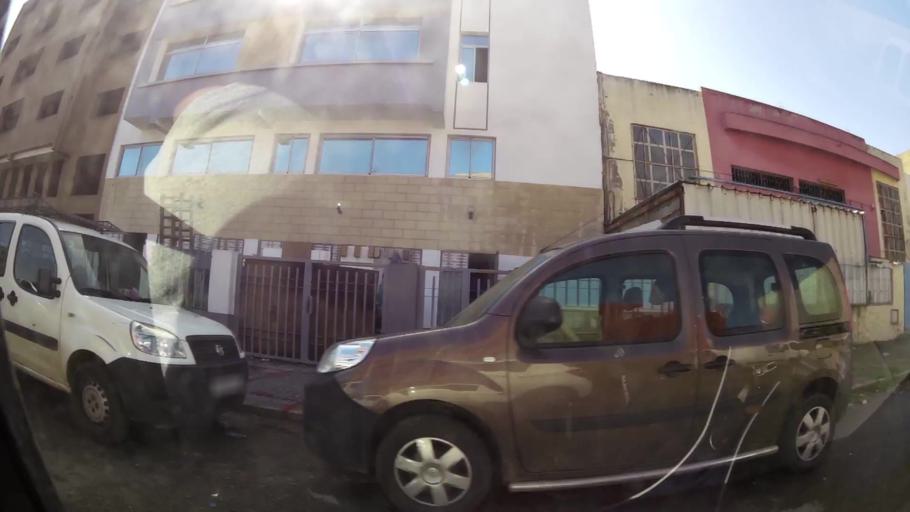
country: MA
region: Grand Casablanca
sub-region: Mediouna
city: Tit Mellil
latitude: 33.6181
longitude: -7.5077
